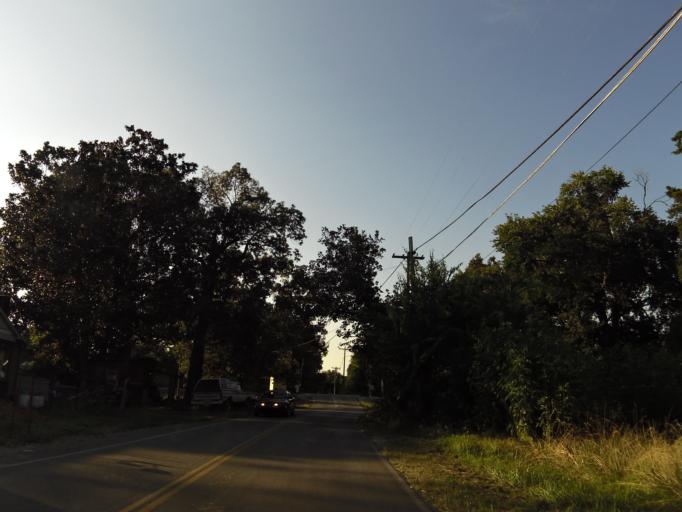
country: US
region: Tennessee
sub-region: McMinn County
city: Englewood
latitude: 35.4219
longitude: -84.4910
